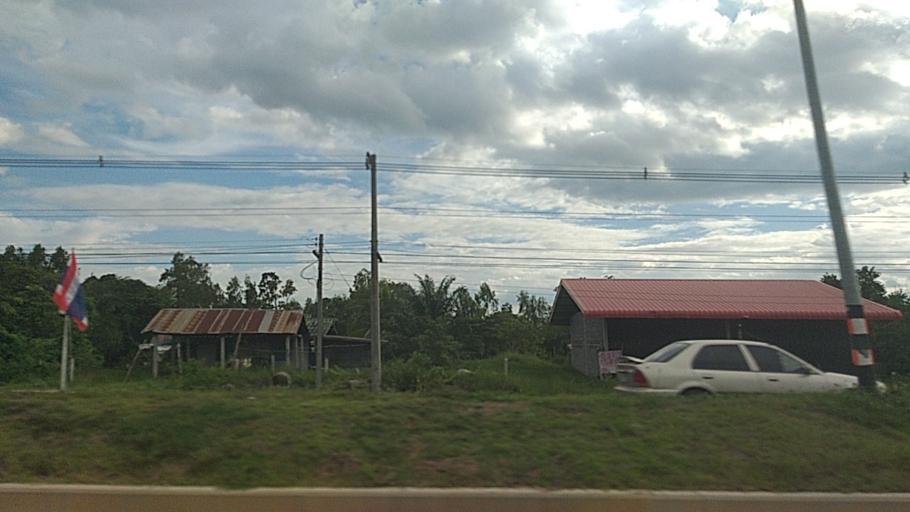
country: TH
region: Surin
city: Kap Choeng
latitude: 14.5582
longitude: 103.5015
